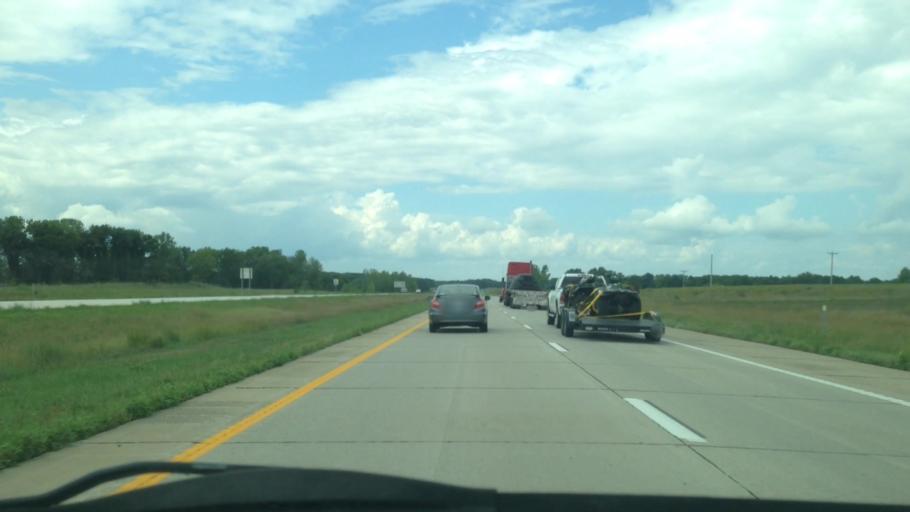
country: US
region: Missouri
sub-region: Pike County
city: Bowling Green
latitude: 39.3742
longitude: -91.2188
